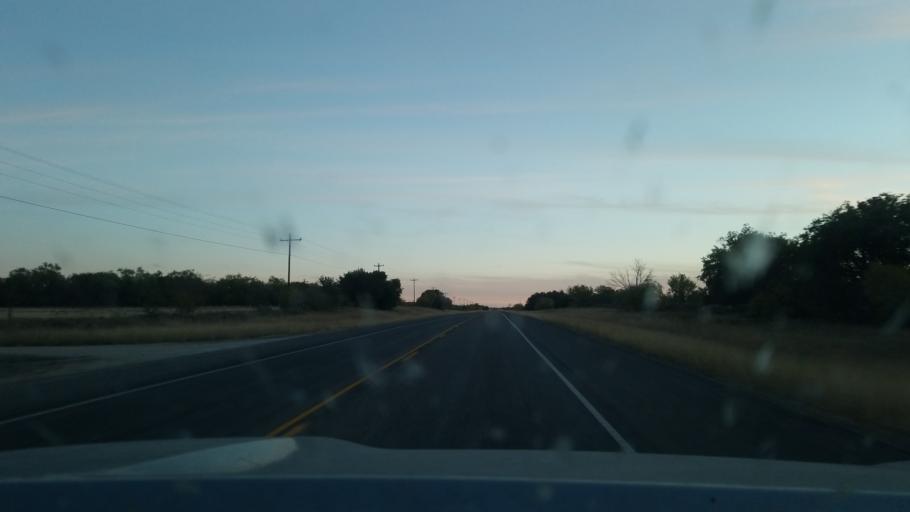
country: US
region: Texas
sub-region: Stephens County
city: Breckenridge
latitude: 32.5750
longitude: -98.8947
